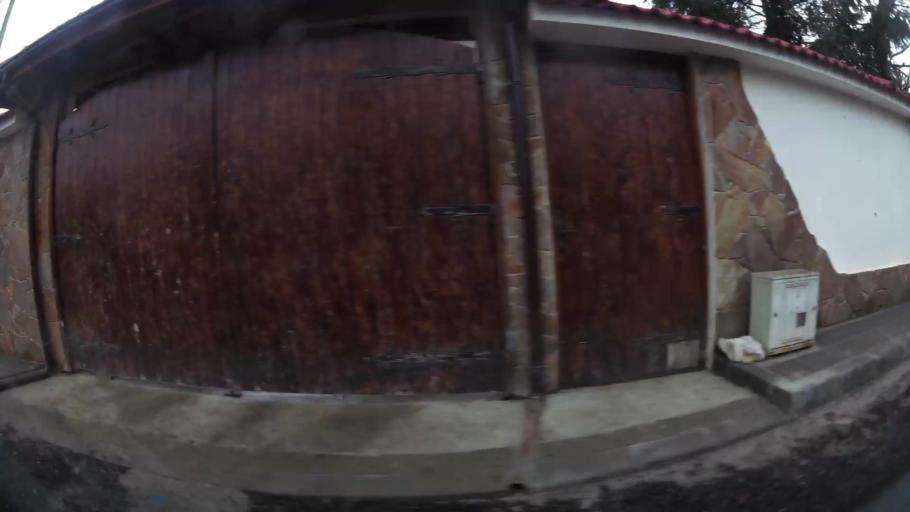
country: BG
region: Sofia-Capital
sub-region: Stolichna Obshtina
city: Sofia
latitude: 42.6185
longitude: 23.3770
